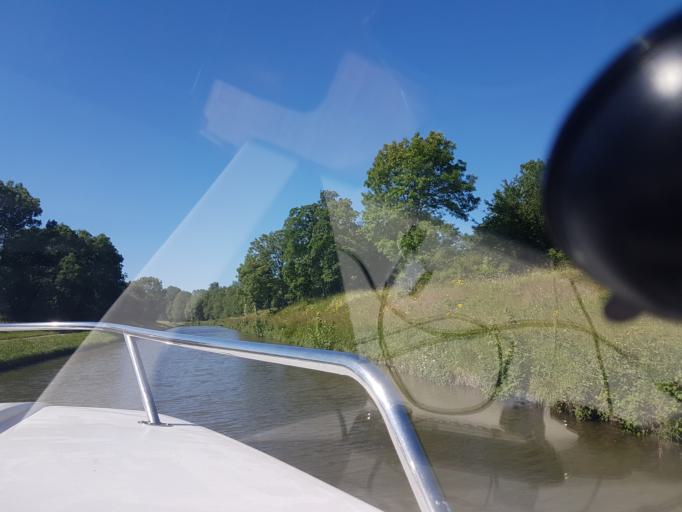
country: FR
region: Bourgogne
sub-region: Departement de la Nievre
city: Clamecy
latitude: 47.5382
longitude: 3.6009
